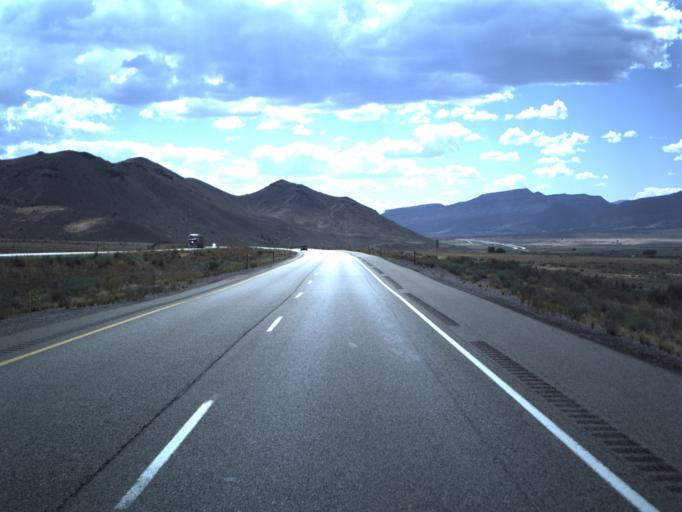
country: US
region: Utah
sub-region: Sevier County
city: Aurora
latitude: 38.8882
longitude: -111.9126
